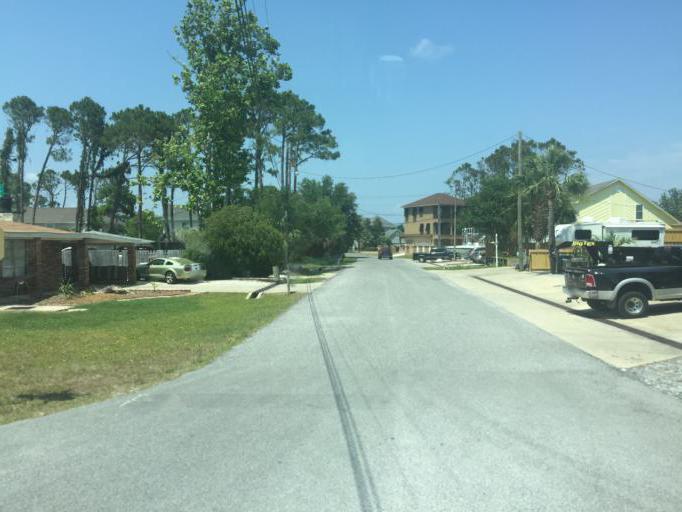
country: US
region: Florida
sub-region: Bay County
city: Lower Grand Lagoon
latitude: 30.1598
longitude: -85.7741
